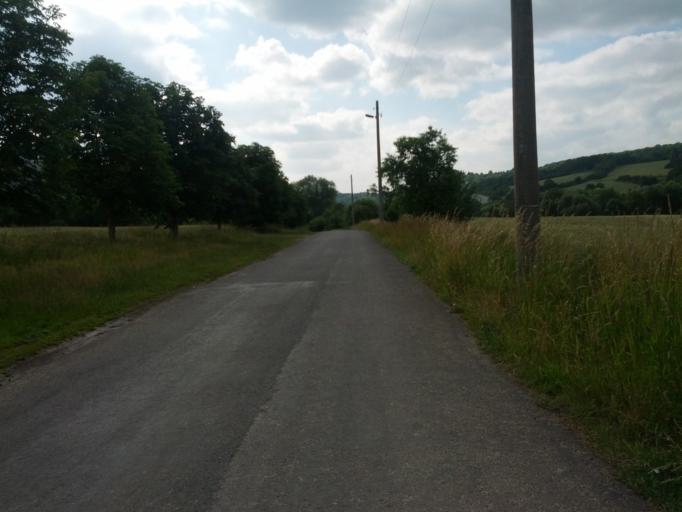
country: DE
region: Thuringia
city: Eisenach
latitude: 50.9775
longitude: 10.3671
